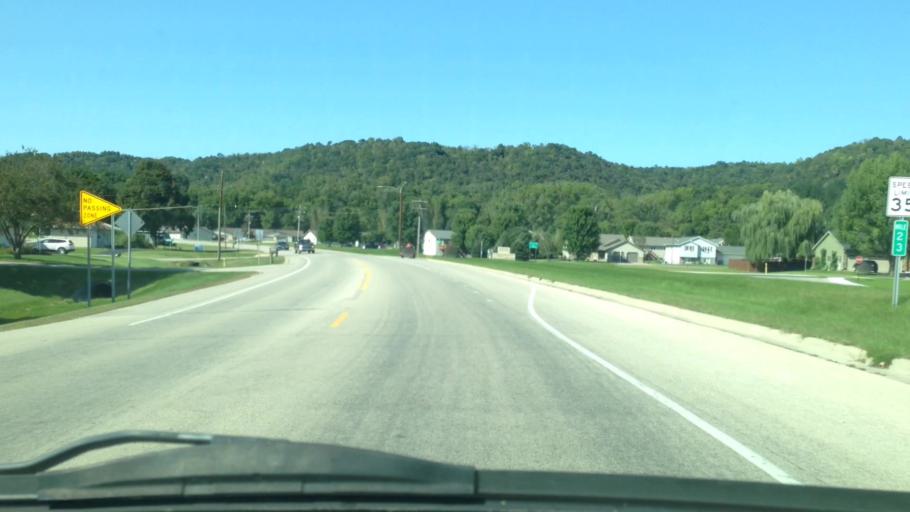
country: US
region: Minnesota
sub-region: Fillmore County
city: Rushford
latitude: 43.8167
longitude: -91.7532
